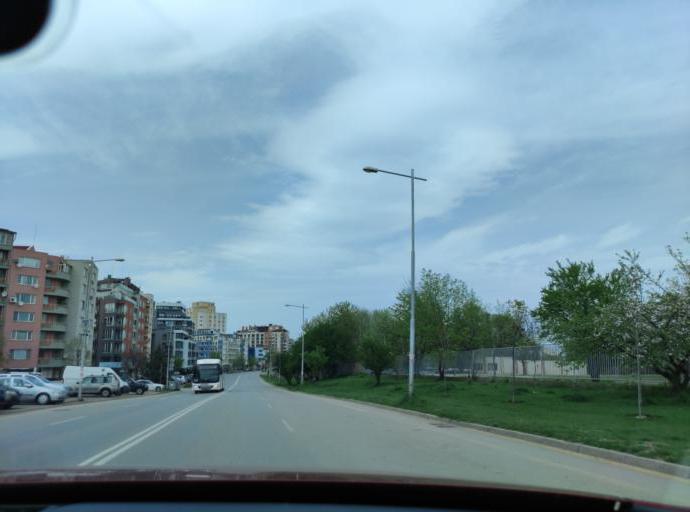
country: BG
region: Sofia-Capital
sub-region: Stolichna Obshtina
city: Sofia
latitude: 42.6449
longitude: 23.3452
